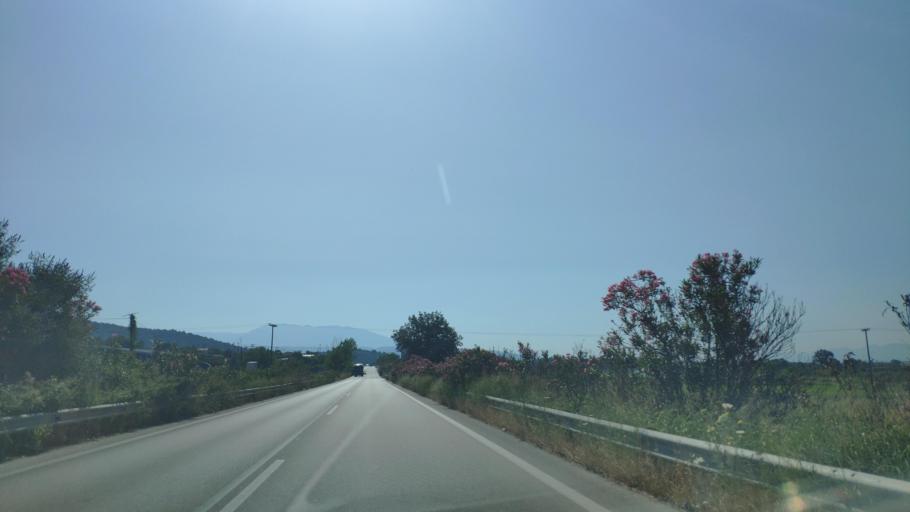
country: GR
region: West Greece
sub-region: Nomos Aitolias kai Akarnanias
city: Fitiai
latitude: 38.6871
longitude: 21.2375
